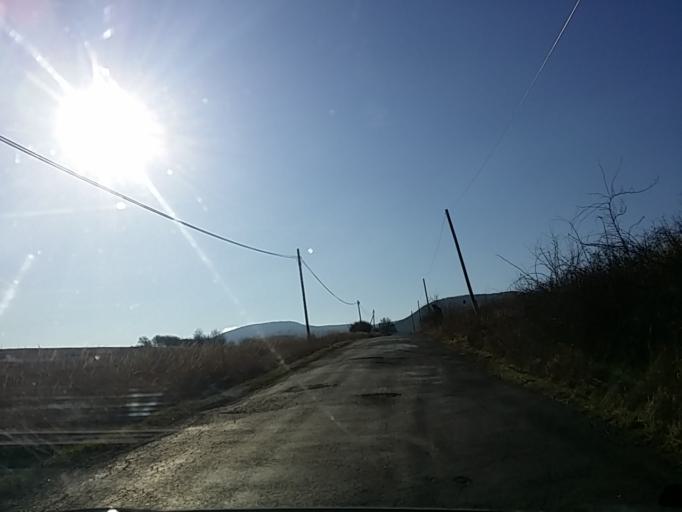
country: HU
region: Heves
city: Szilvasvarad
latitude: 48.1628
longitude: 20.4919
